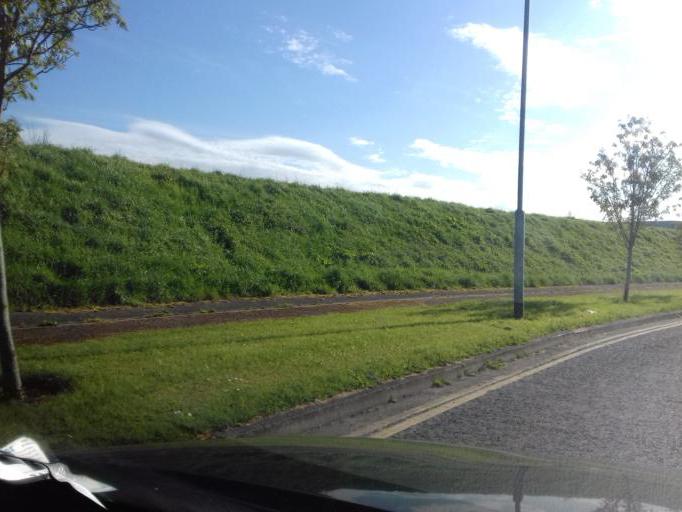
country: IE
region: Leinster
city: Castleknock
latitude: 53.3961
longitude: -6.3384
